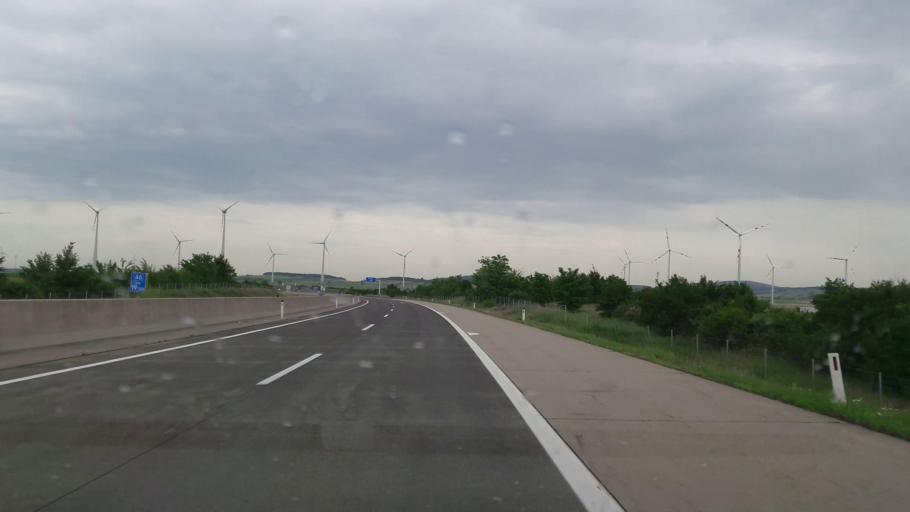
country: AT
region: Lower Austria
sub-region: Politischer Bezirk Bruck an der Leitha
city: Berg
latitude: 48.0817
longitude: 17.0417
